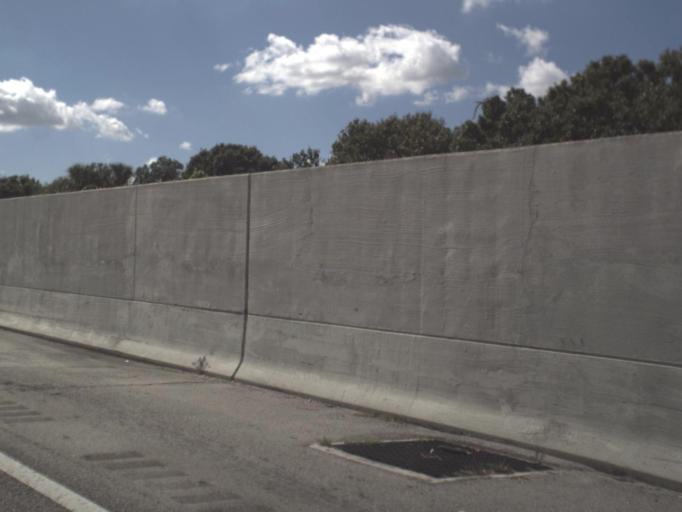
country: US
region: Florida
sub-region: Broward County
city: Lauderdale Lakes
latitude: 26.1853
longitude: -80.2167
